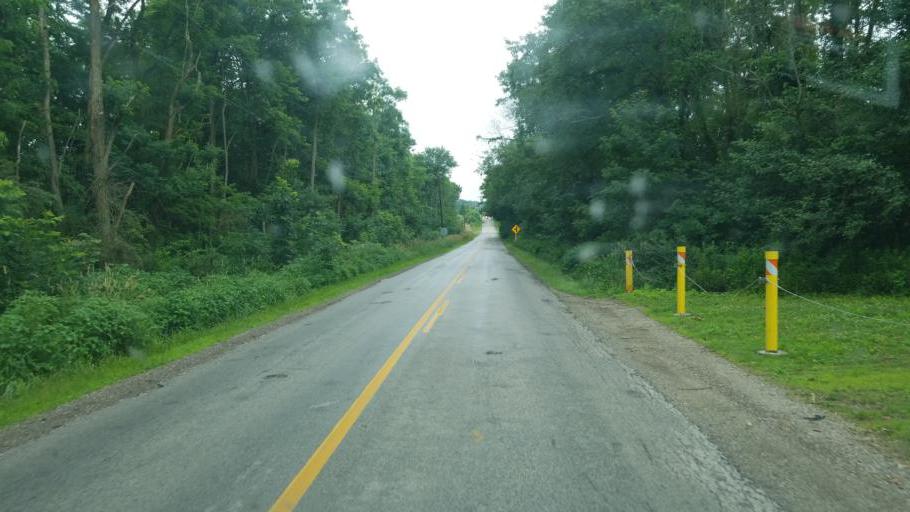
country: US
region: Ohio
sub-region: Wayne County
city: Dalton
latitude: 40.8428
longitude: -81.6480
